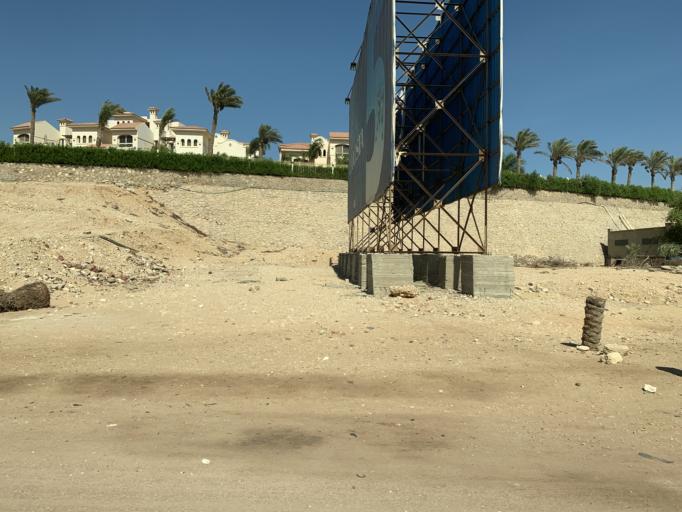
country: EG
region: As Suways
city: Ain Sukhna
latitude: 29.2217
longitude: 32.6208
